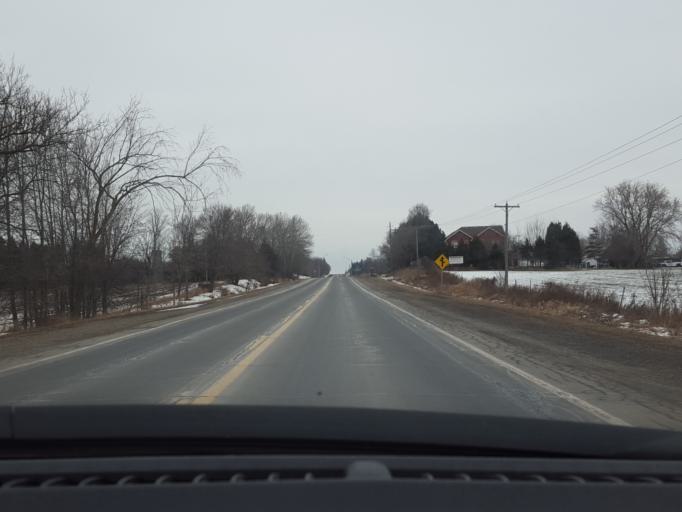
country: CA
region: Ontario
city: Newmarket
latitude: 44.1220
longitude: -79.4204
